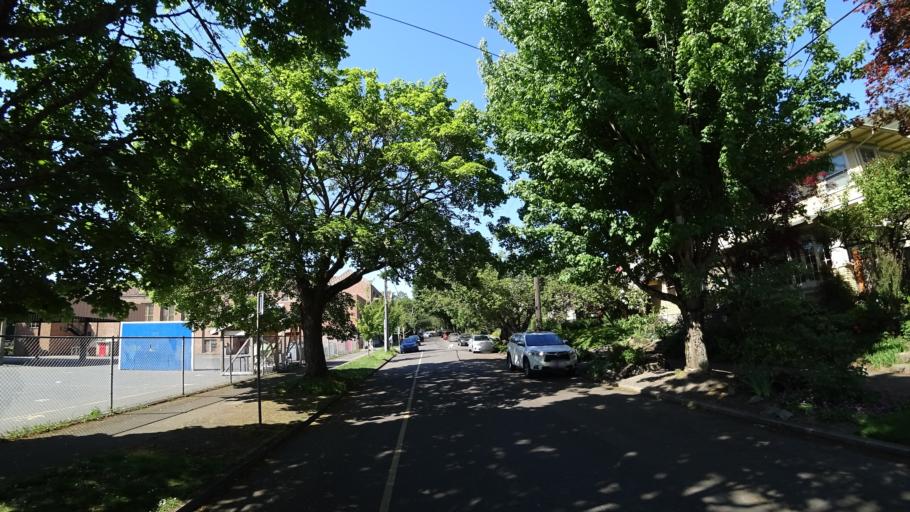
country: US
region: Oregon
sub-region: Multnomah County
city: Portland
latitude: 45.5395
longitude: -122.6515
